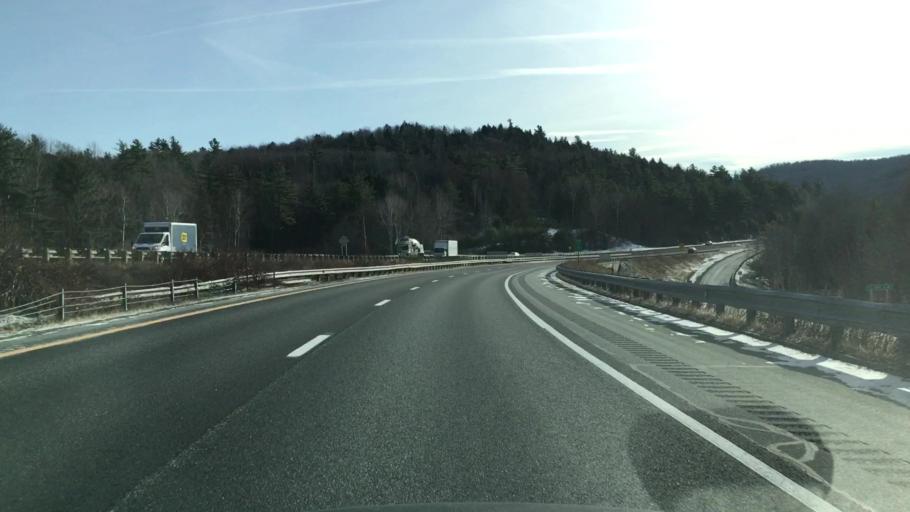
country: US
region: New Hampshire
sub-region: Grafton County
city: Enfield
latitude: 43.5987
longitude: -72.1661
